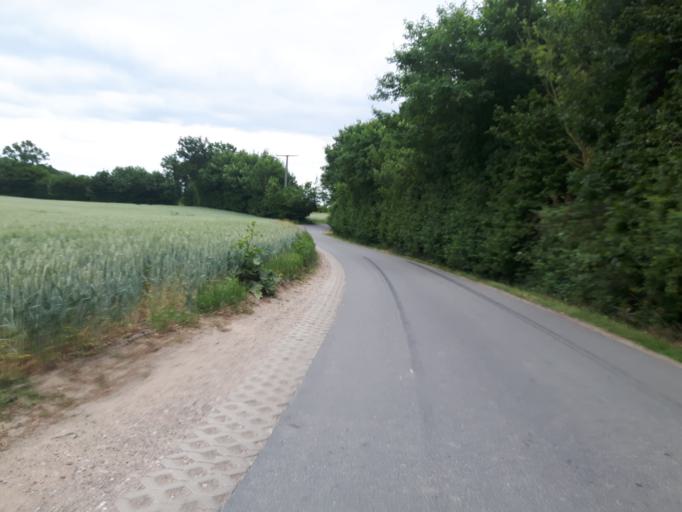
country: DE
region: Schleswig-Holstein
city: Schashagen
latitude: 54.1234
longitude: 10.9070
